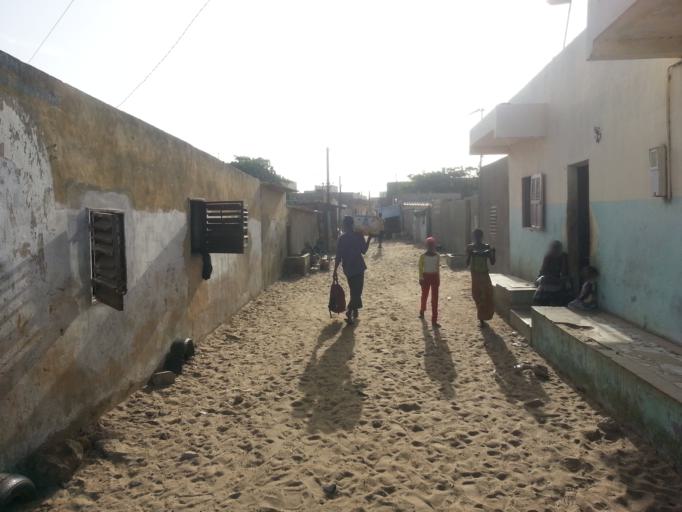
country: SN
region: Dakar
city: Pikine
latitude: 14.7719
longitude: -17.3777
